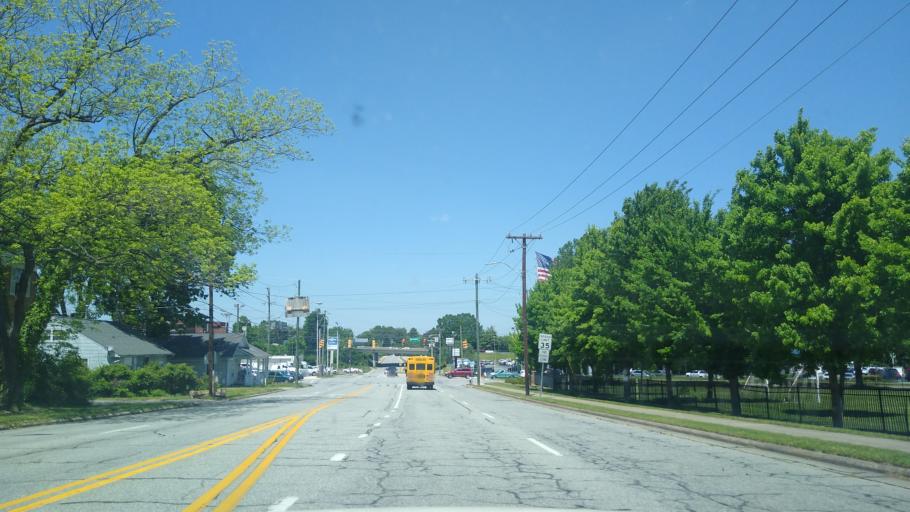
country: US
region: North Carolina
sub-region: Guilford County
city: Greensboro
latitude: 36.0847
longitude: -79.7827
